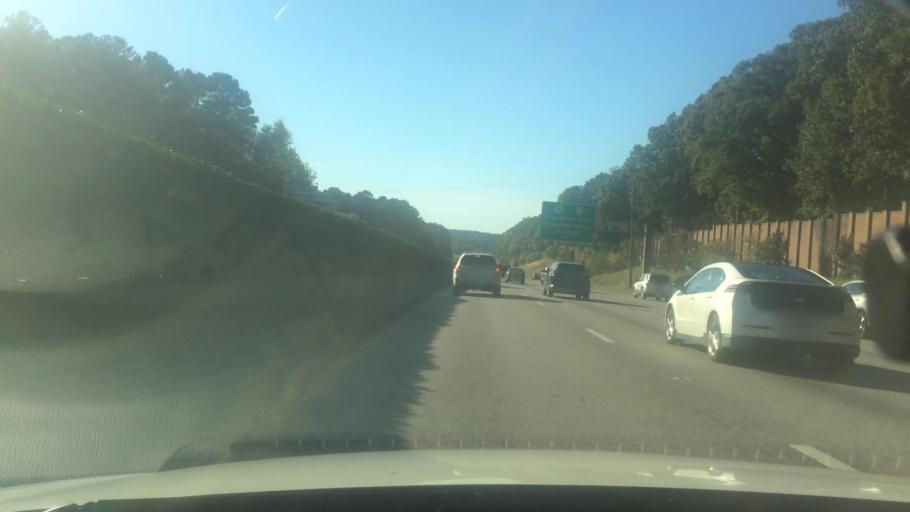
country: US
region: North Carolina
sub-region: Wake County
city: West Raleigh
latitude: 35.8358
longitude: -78.6486
